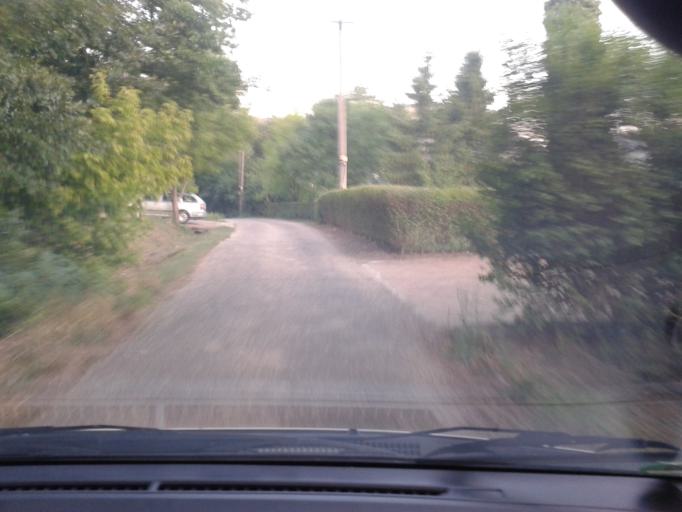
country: HU
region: Komarom-Esztergom
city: Esztergom
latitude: 47.8280
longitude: 18.7947
